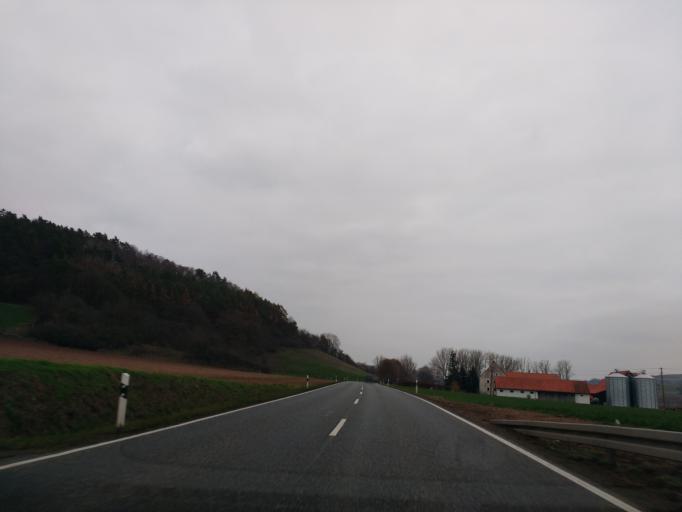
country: DE
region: Hesse
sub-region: Regierungsbezirk Kassel
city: Alheim
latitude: 51.0570
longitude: 9.6347
